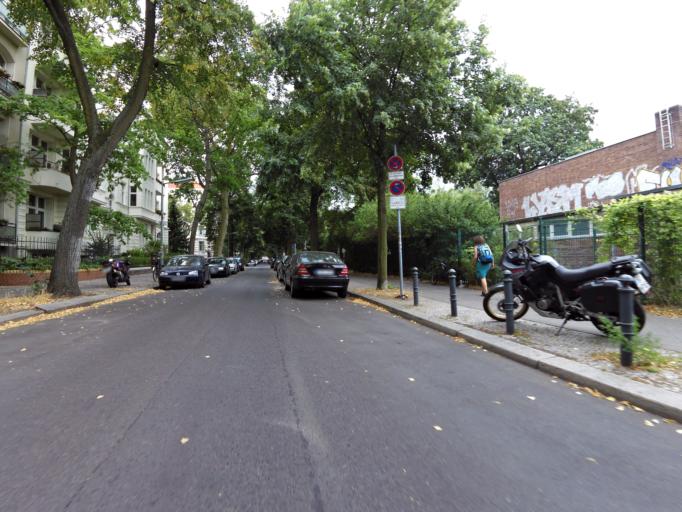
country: DE
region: Berlin
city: Friedenau
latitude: 52.4763
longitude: 13.3353
